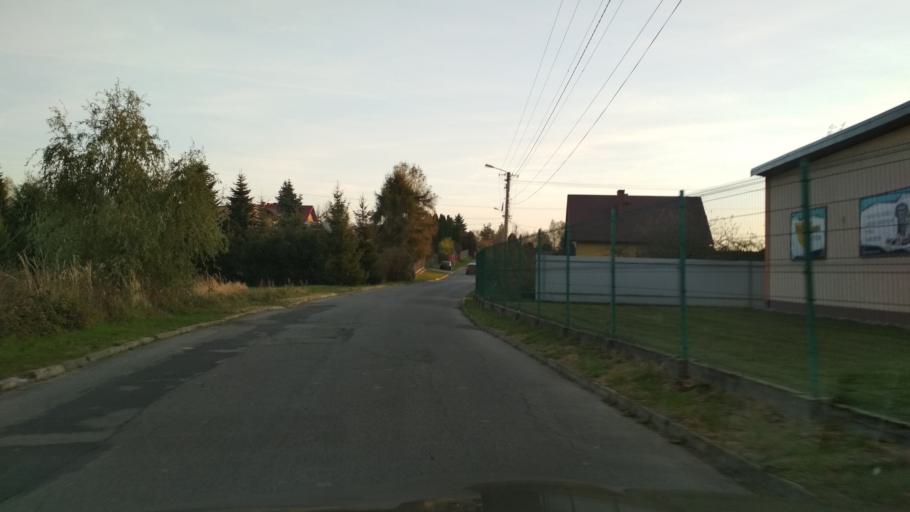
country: PL
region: Subcarpathian Voivodeship
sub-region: Powiat ropczycko-sedziszowski
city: Sedziszow Malopolski
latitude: 50.0654
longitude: 21.7109
